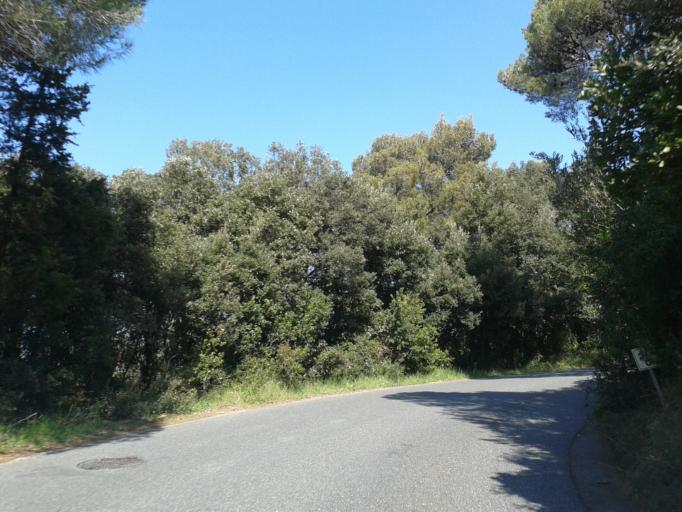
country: IT
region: Tuscany
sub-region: Provincia di Livorno
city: Quercianella
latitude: 43.4495
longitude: 10.3824
